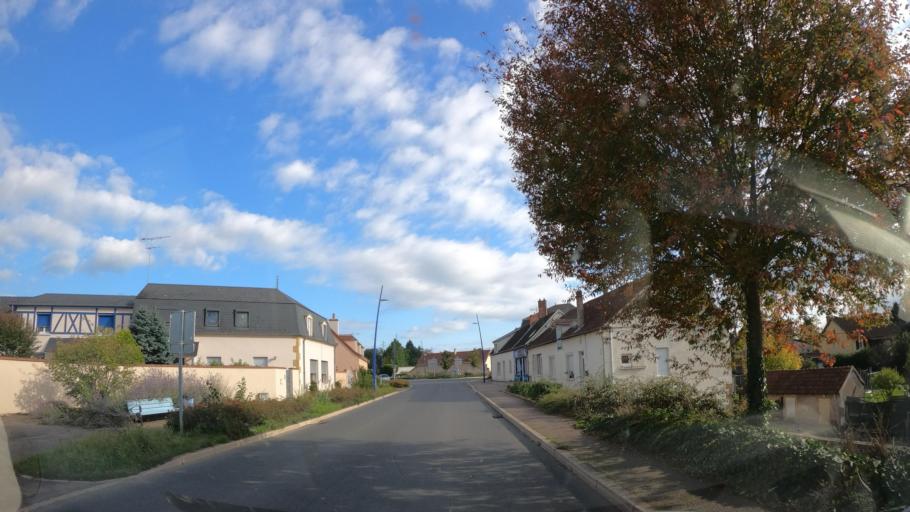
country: FR
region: Auvergne
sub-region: Departement de l'Allier
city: Dompierre-sur-Besbre
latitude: 46.5172
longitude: 3.6879
